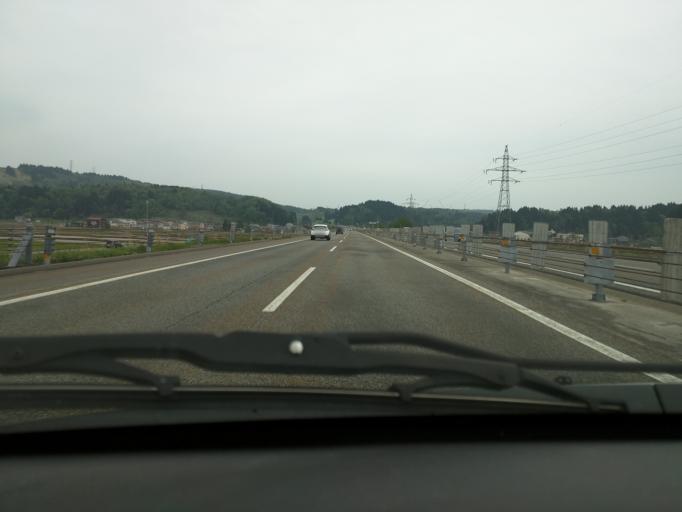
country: JP
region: Niigata
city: Ojiya
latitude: 37.2937
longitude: 138.7828
